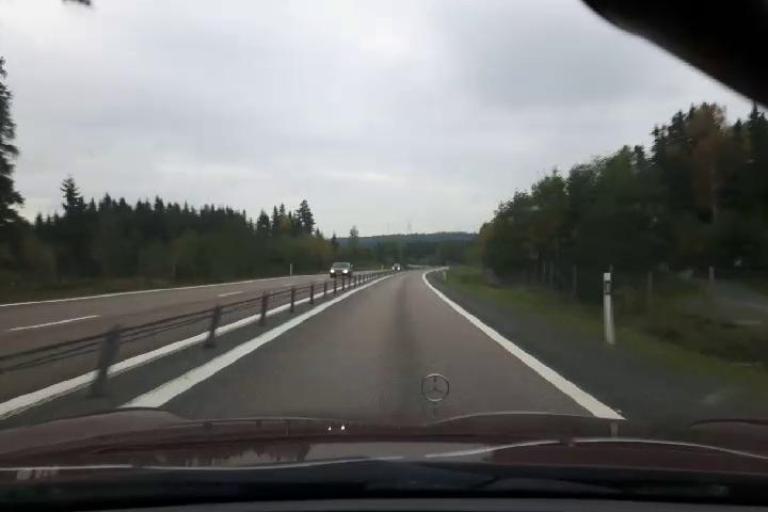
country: SE
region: Vaesternorrland
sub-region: Kramfors Kommun
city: Nordingra
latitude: 62.9130
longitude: 18.0933
